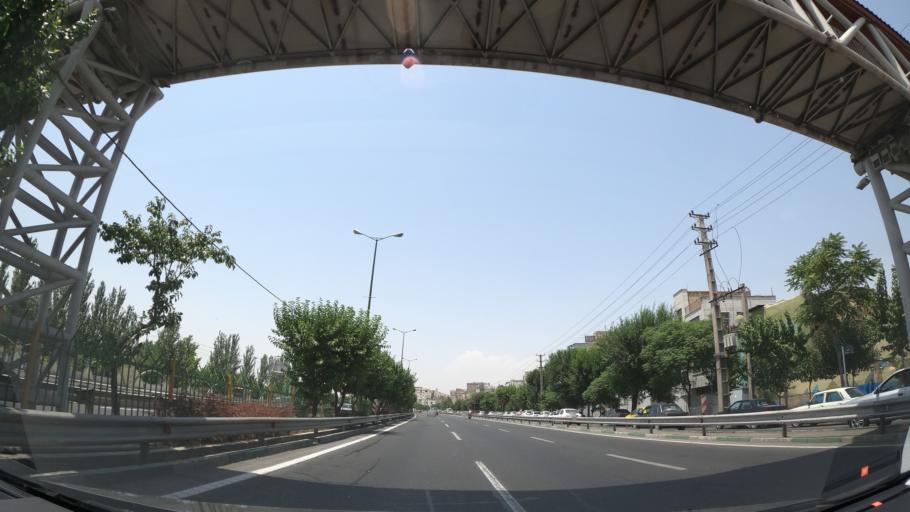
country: IR
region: Tehran
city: Tehran
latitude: 35.6491
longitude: 51.3897
